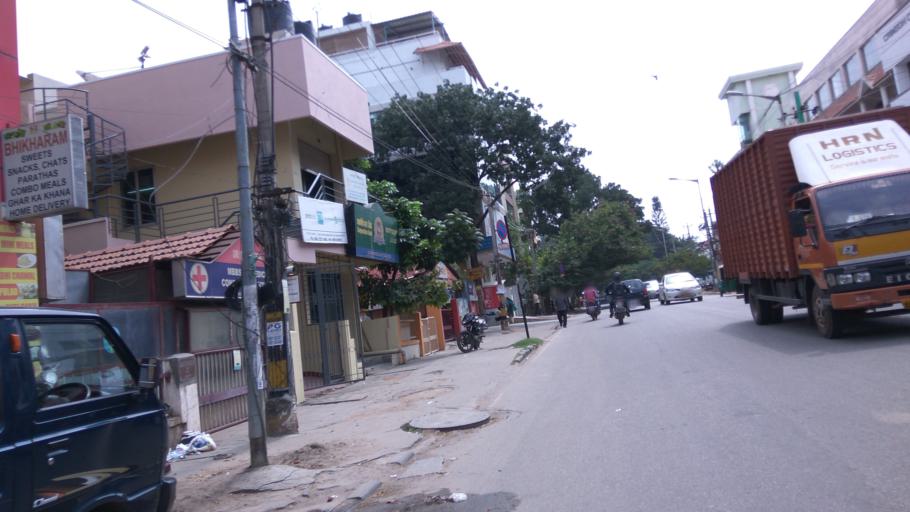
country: IN
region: Karnataka
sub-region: Bangalore Urban
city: Bangalore
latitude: 12.9679
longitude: 77.6534
